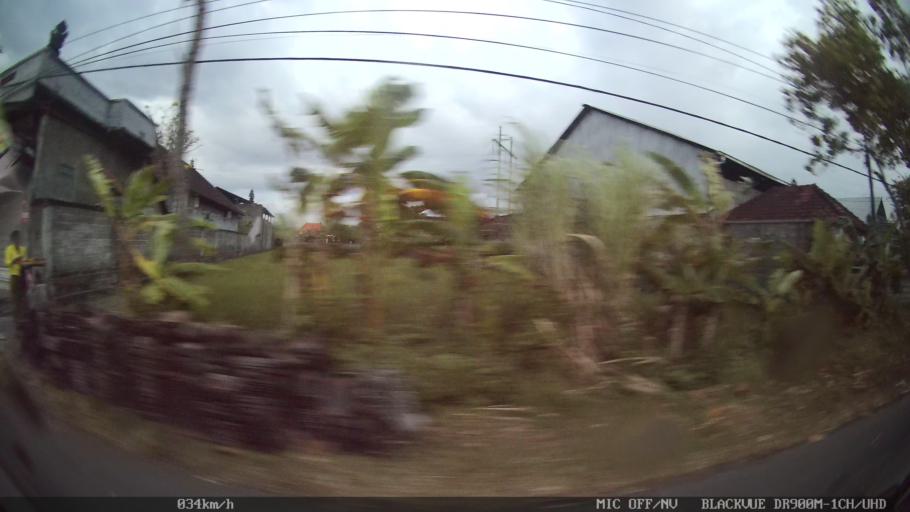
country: ID
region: Bali
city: Banjar Pasekan
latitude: -8.6391
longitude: 115.2822
